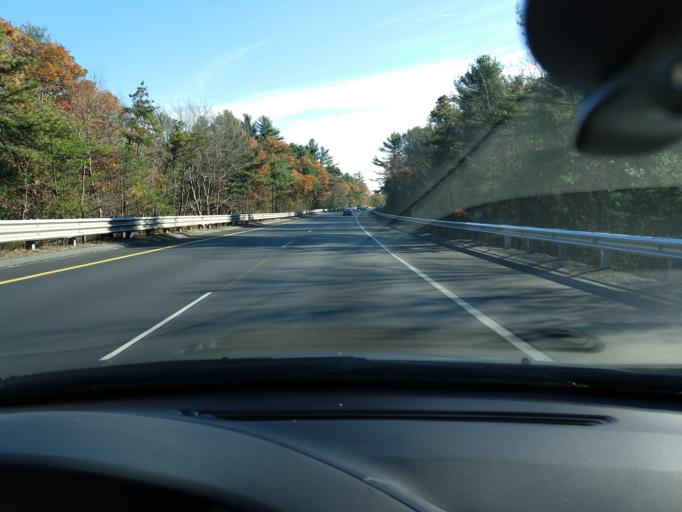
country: US
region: Massachusetts
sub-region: Plymouth County
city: Plymouth
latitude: 41.9270
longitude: -70.6334
